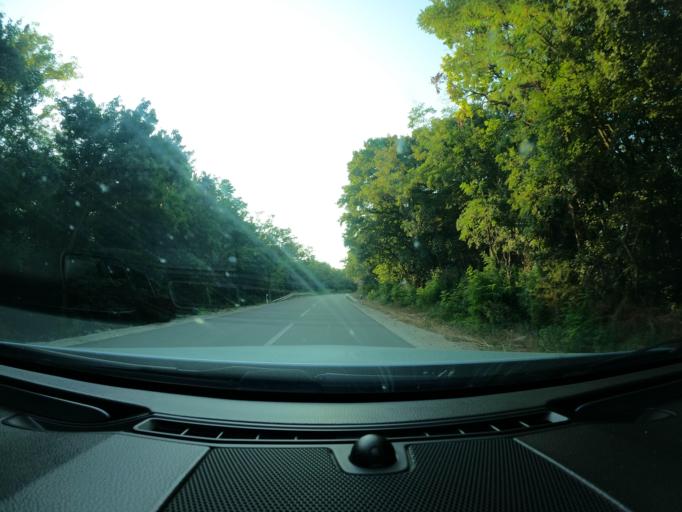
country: RS
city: Vrdnik
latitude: 45.1246
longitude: 19.7279
